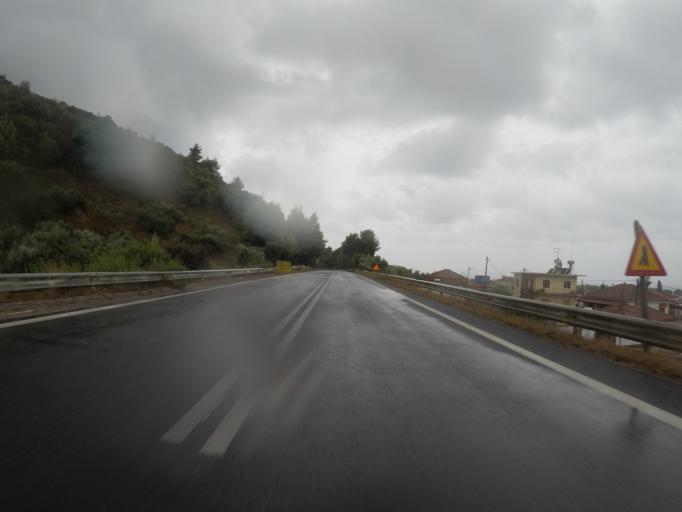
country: GR
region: West Greece
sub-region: Nomos Ileias
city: Zacharo
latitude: 37.3770
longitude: 21.6935
